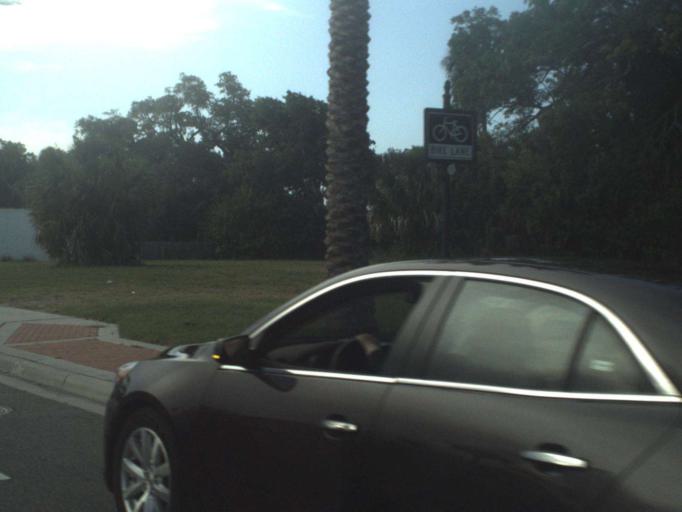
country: US
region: Florida
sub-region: Volusia County
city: South Daytona
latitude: 29.1792
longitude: -81.0059
